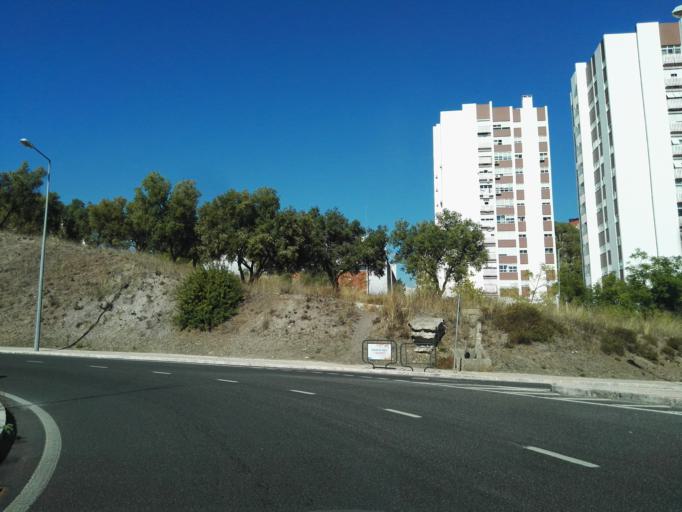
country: PT
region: Lisbon
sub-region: Odivelas
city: Povoa de Santo Adriao
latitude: 38.8082
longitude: -9.1628
